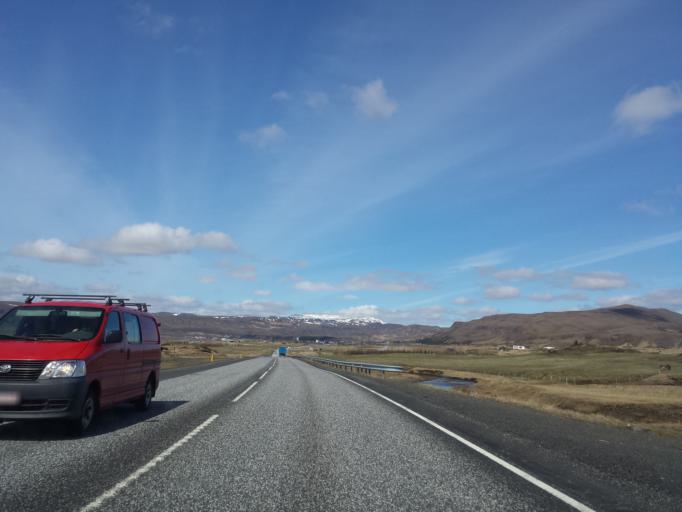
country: IS
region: South
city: Hveragerdi
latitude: 63.9724
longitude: -21.1392
